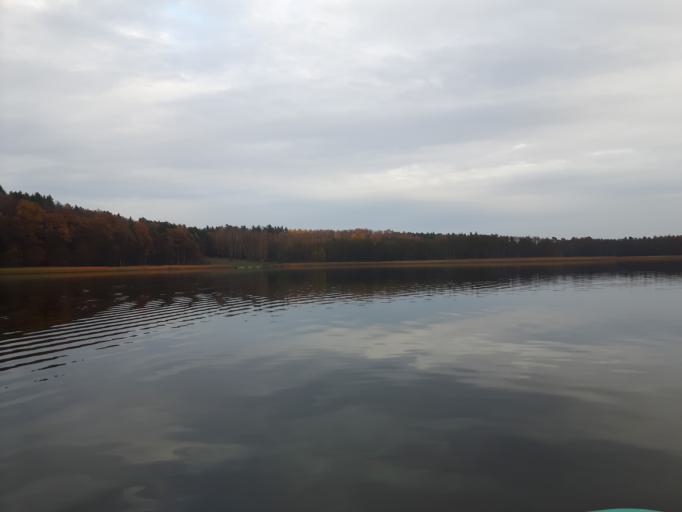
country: PL
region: Warmian-Masurian Voivodeship
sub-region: Powiat olsztynski
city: Barczewo
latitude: 53.8281
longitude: 20.7347
